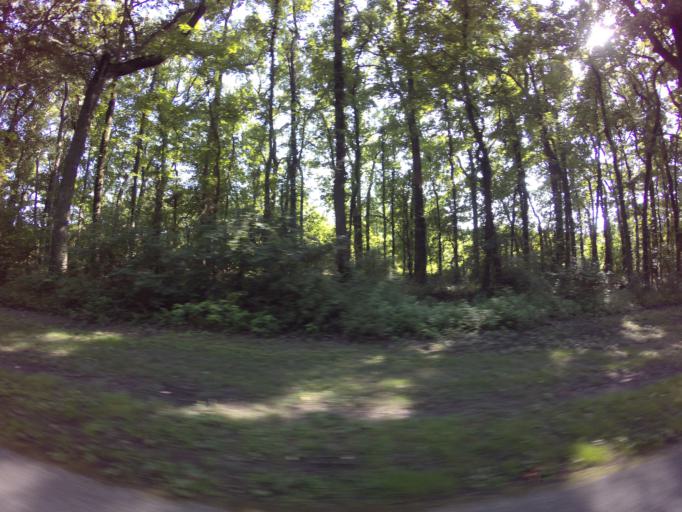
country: US
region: Maryland
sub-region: Baltimore County
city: Edgemere
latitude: 39.2166
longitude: -76.4264
